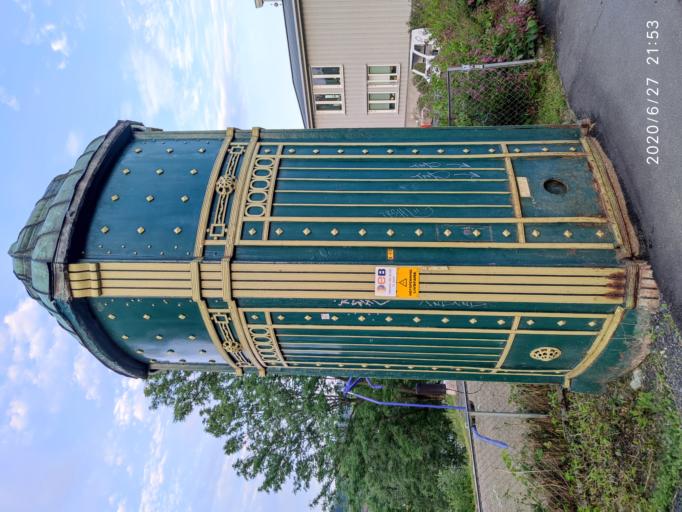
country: NO
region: Buskerud
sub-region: Kongsberg
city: Kongsberg
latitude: 59.6648
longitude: 9.6504
